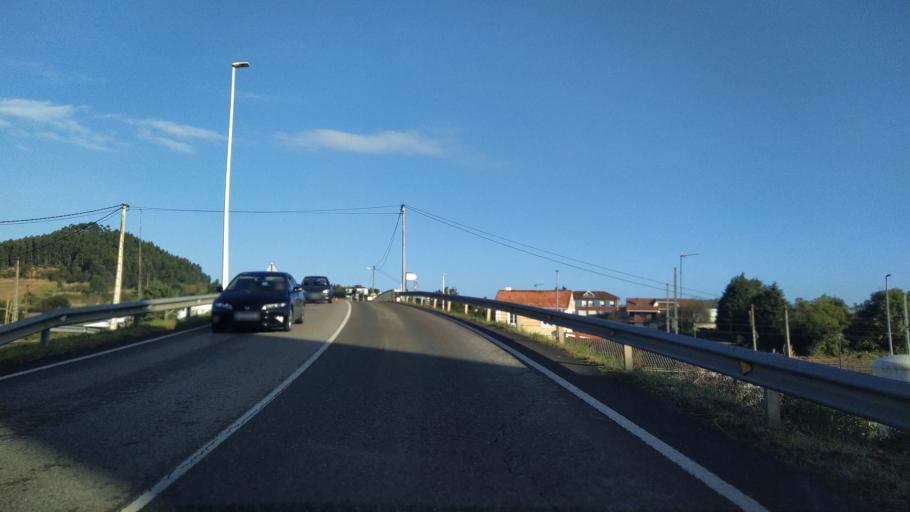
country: ES
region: Cantabria
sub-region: Provincia de Cantabria
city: Santa Cruz de Bezana
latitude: 43.4346
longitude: -3.9180
